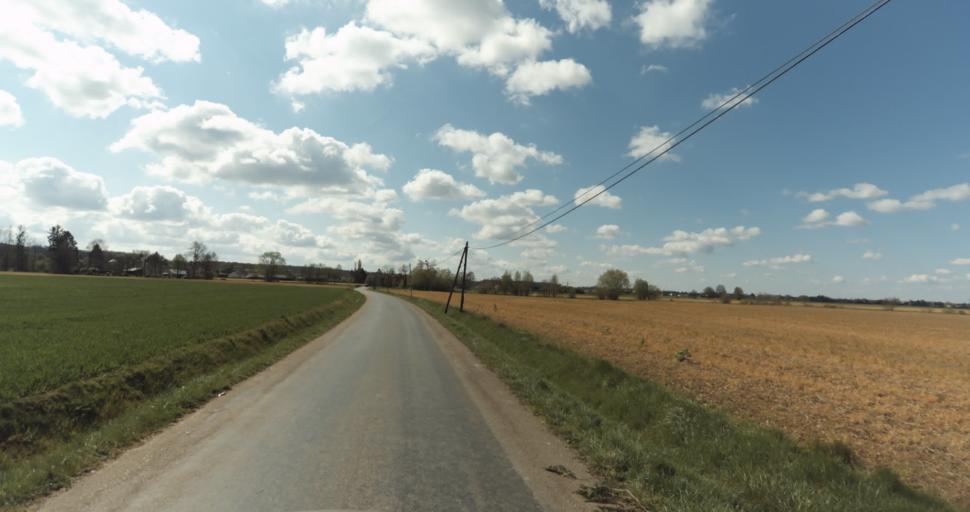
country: FR
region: Bourgogne
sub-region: Departement de la Cote-d'Or
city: Auxonne
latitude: 47.2050
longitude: 5.4235
